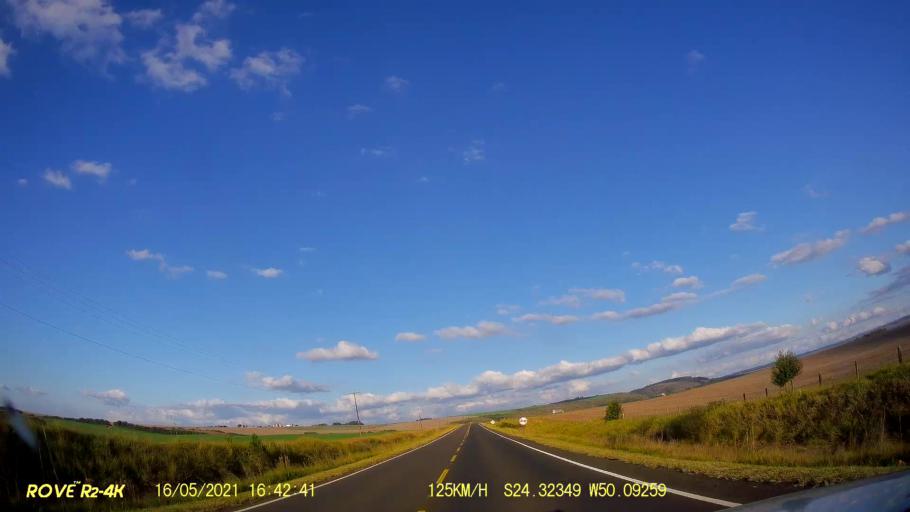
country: BR
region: Parana
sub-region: Pirai Do Sul
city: Pirai do Sul
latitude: -24.3240
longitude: -50.0925
